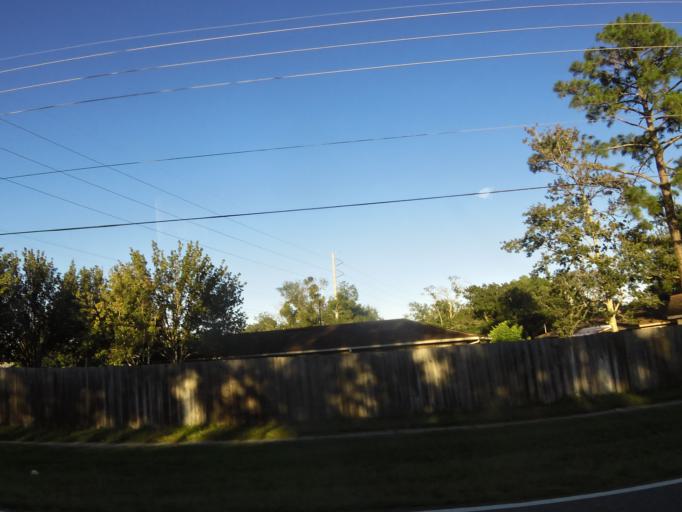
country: US
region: Florida
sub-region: Duval County
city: Neptune Beach
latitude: 30.3030
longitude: -81.4439
